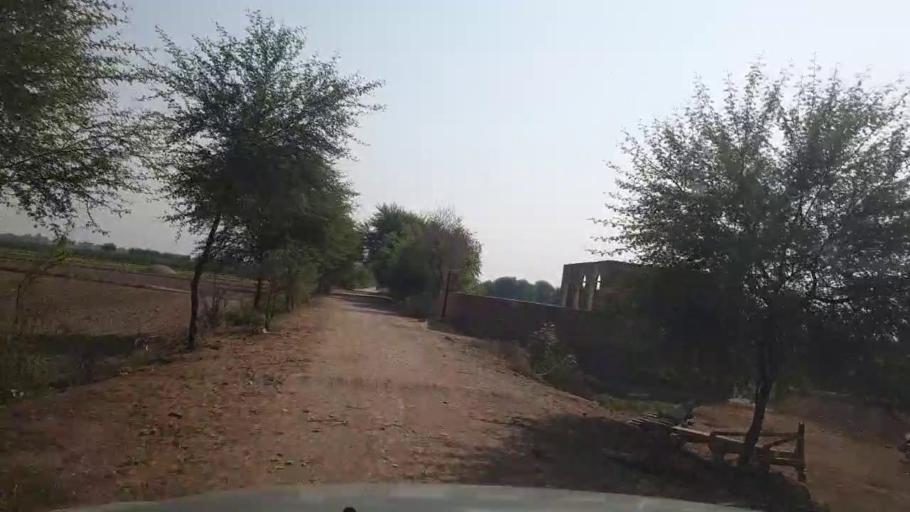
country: PK
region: Sindh
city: Bhit Shah
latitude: 25.7357
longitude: 68.4972
